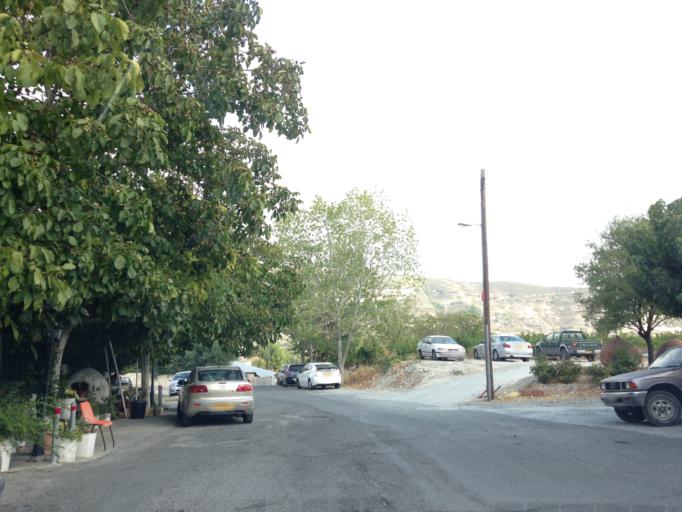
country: CY
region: Limassol
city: Pachna
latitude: 34.8471
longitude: 32.8081
